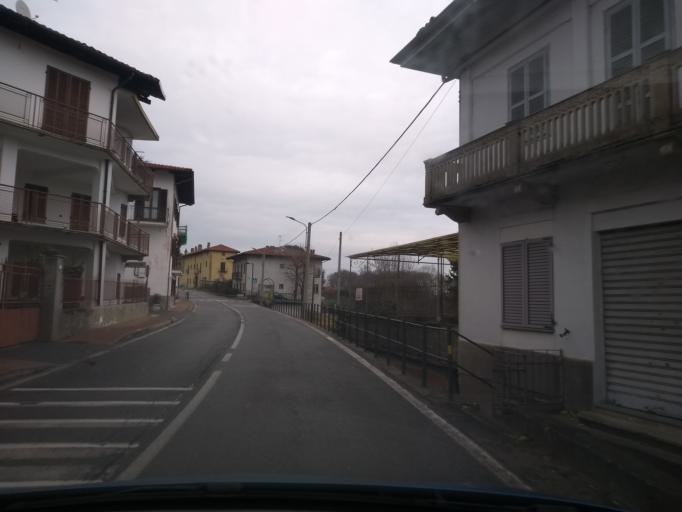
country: IT
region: Piedmont
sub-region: Provincia di Torino
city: Quagliuzzo
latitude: 45.4261
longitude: 7.7812
